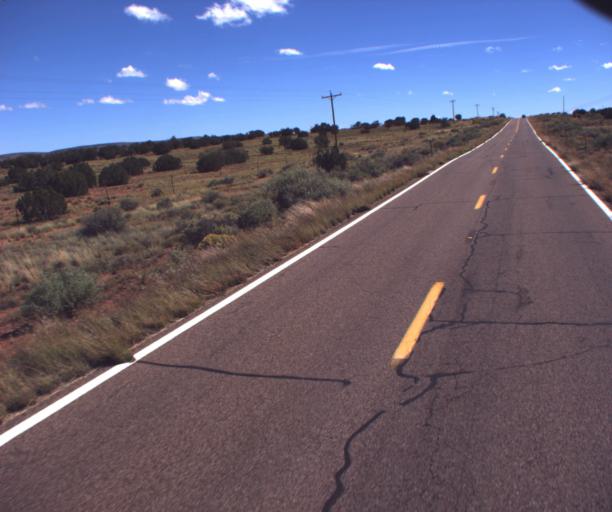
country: US
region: Arizona
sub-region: Apache County
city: Saint Johns
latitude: 34.5625
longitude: -109.6300
